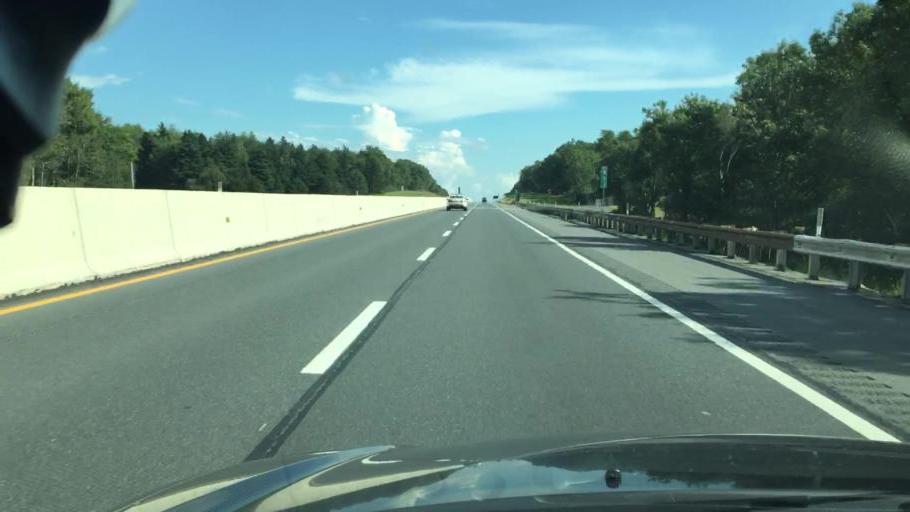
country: US
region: Pennsylvania
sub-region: Carbon County
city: Towamensing Trails
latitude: 41.0363
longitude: -75.6598
